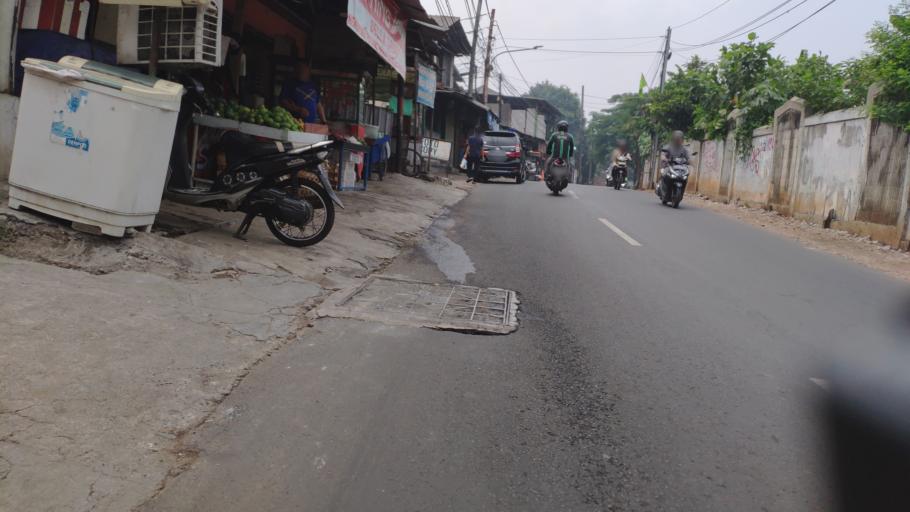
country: ID
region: Jakarta Raya
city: Jakarta
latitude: -6.3063
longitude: 106.8277
